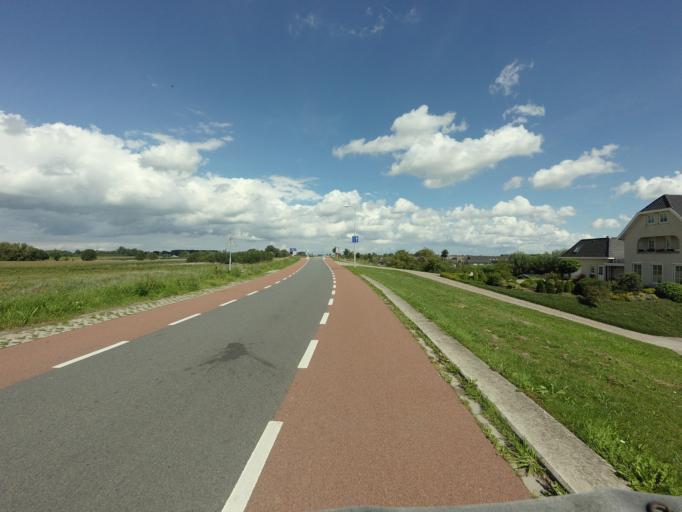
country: NL
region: Utrecht
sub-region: Gemeente Lopik
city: Lopik
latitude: 51.9580
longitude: 4.9760
